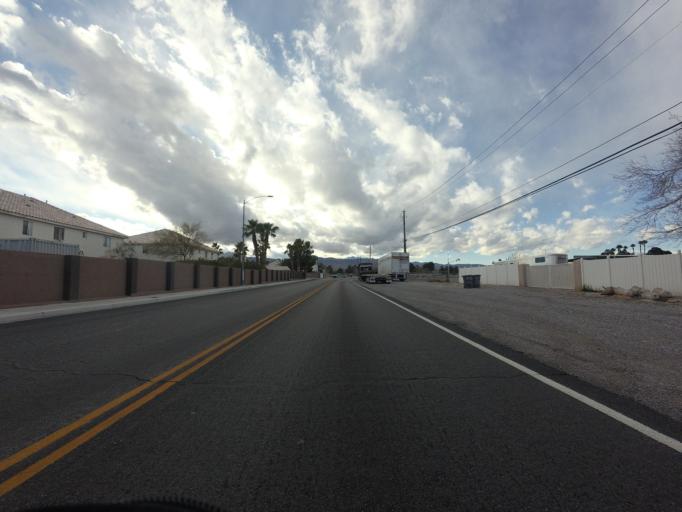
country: US
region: Nevada
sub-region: Clark County
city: Las Vegas
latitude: 36.2699
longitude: -115.2504
